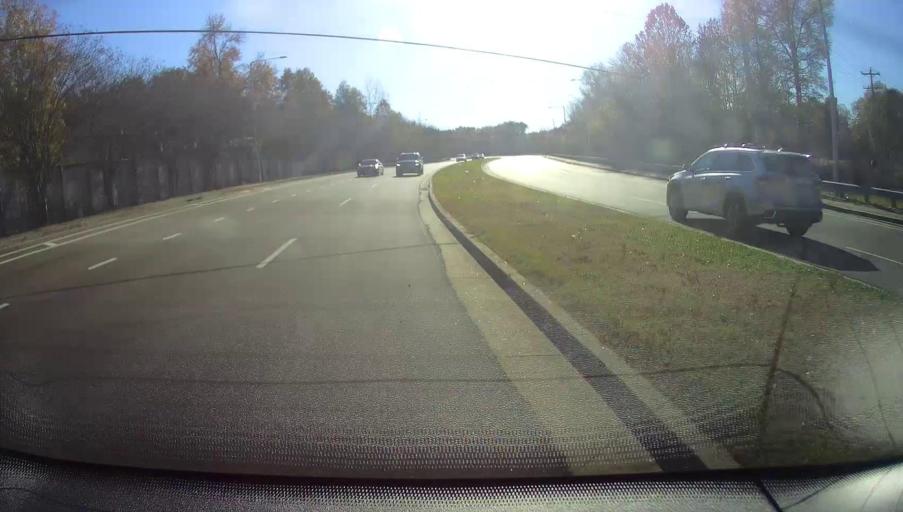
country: US
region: Tennessee
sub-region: Shelby County
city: Germantown
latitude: 35.0814
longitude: -89.8406
